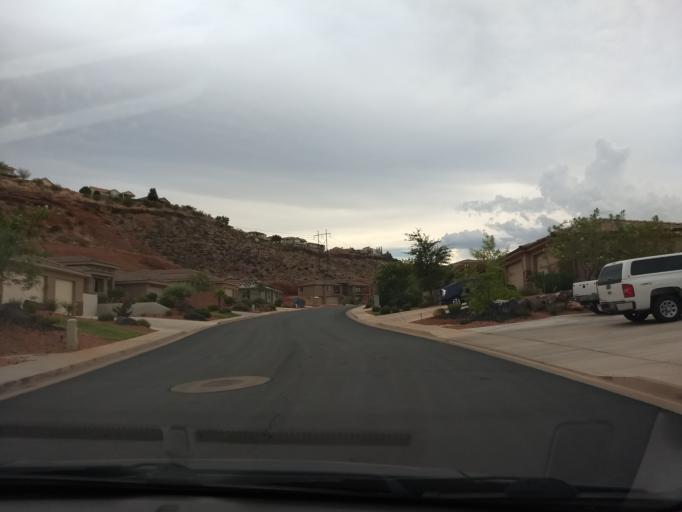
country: US
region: Utah
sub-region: Washington County
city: Saint George
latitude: 37.1093
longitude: -113.5474
